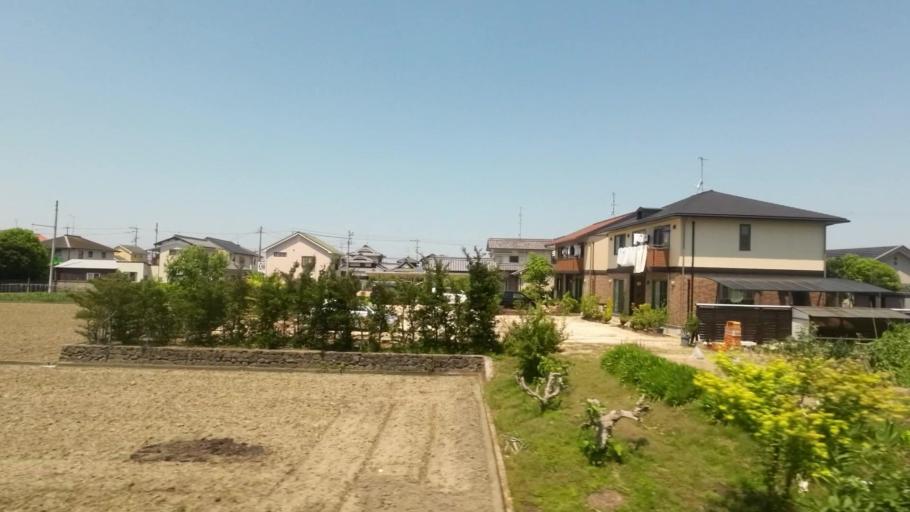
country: JP
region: Ehime
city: Hojo
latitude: 33.9400
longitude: 132.7692
